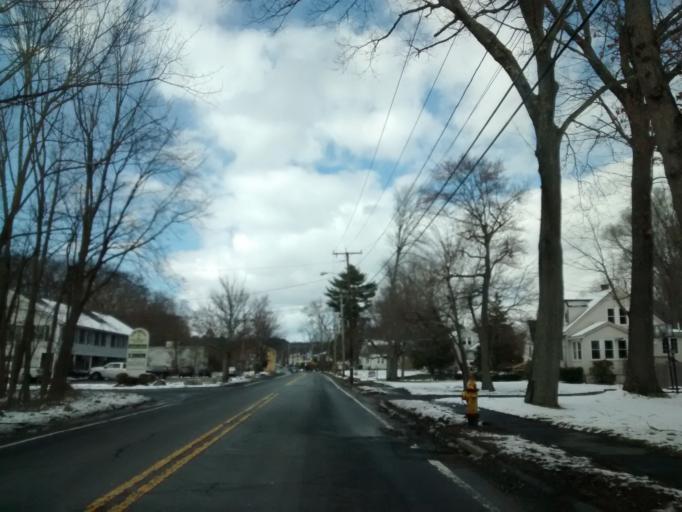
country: US
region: Massachusetts
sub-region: Worcester County
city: Whitinsville
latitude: 42.1212
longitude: -71.6430
